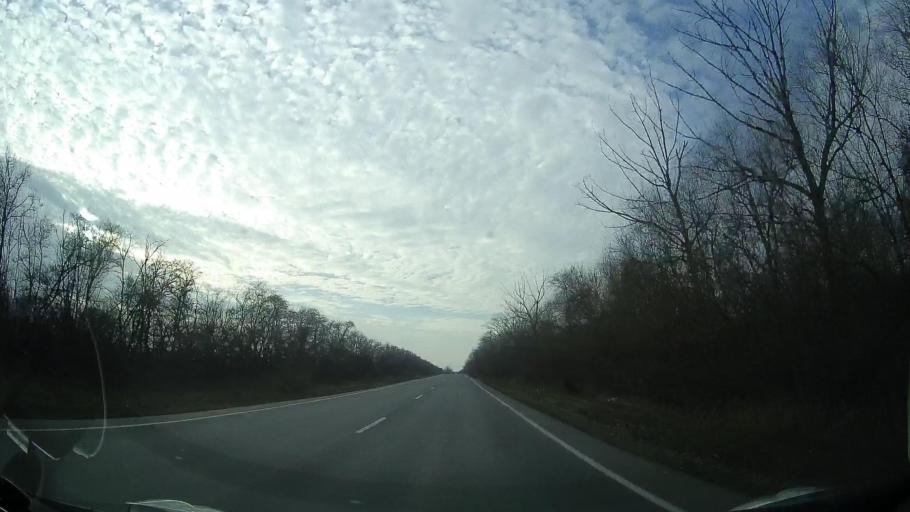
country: RU
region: Rostov
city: Bagayevskaya
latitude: 47.0961
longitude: 40.2922
